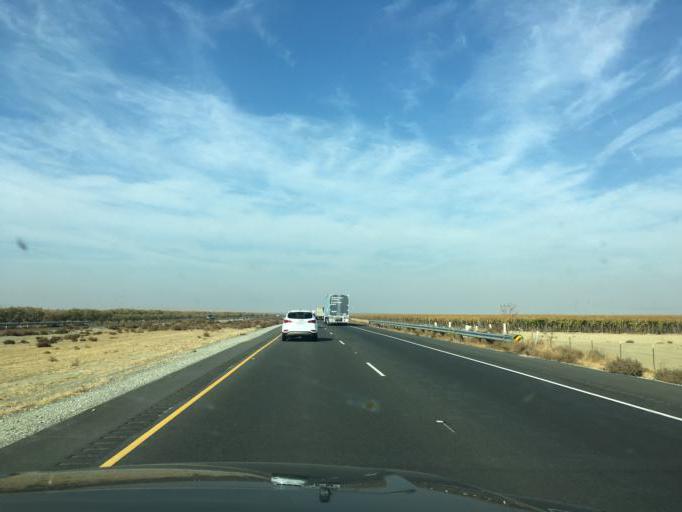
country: US
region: California
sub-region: Kings County
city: Kettleman City
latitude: 35.9060
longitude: -119.8827
